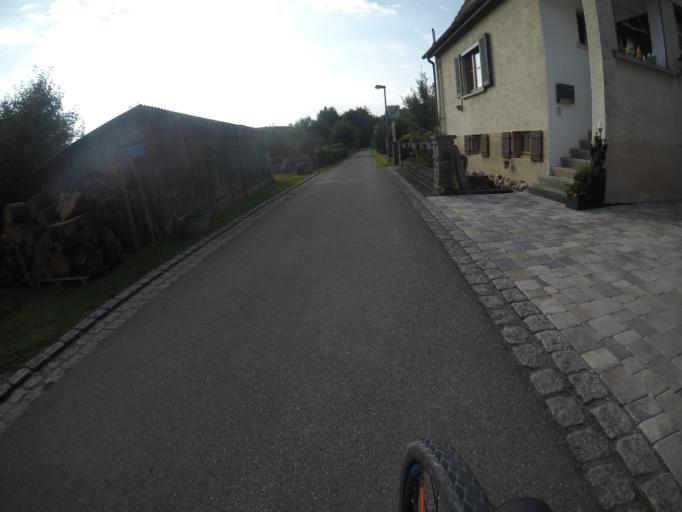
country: DE
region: Baden-Wuerttemberg
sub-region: Regierungsbezirk Stuttgart
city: Neckartenzlingen
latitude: 48.5864
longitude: 9.2406
